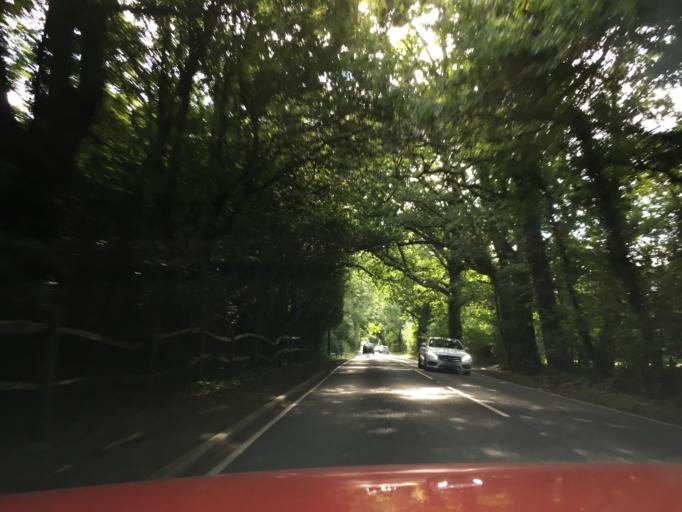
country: GB
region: England
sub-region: West Sussex
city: Southwater
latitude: 51.0552
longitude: -0.3981
